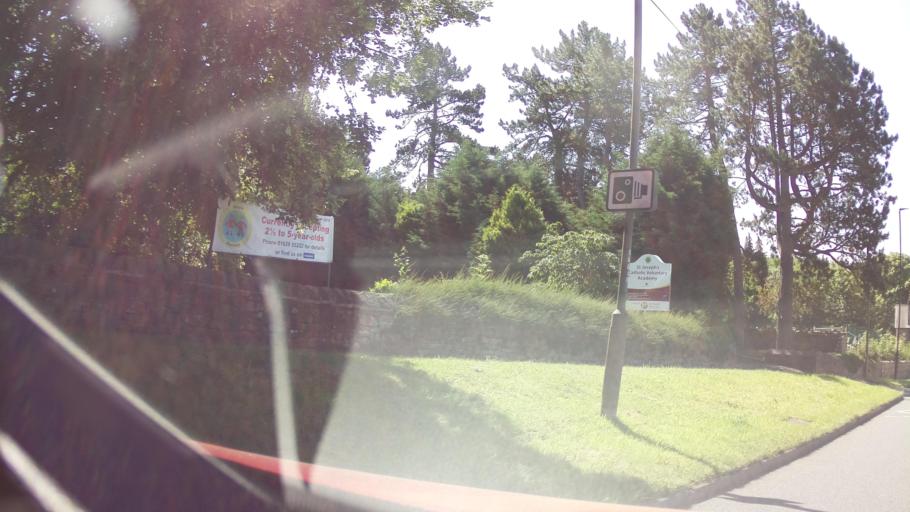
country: GB
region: England
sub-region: Derbyshire
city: Matlock
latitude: 53.1423
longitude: -1.5441
